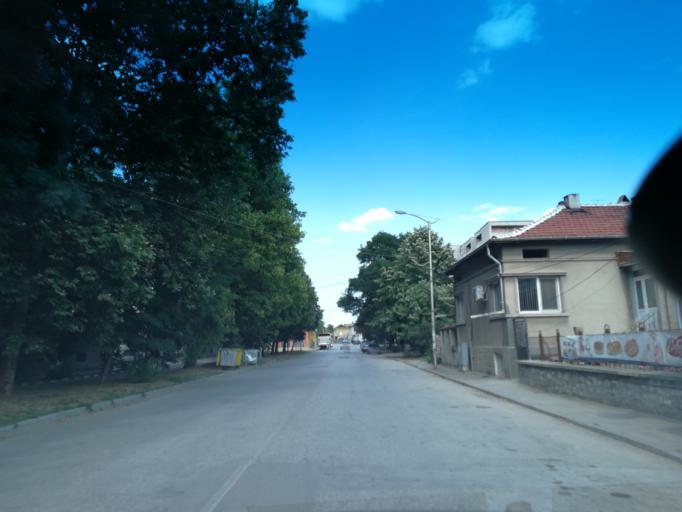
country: BG
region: Stara Zagora
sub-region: Obshtina Chirpan
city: Chirpan
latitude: 42.1984
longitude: 25.3314
